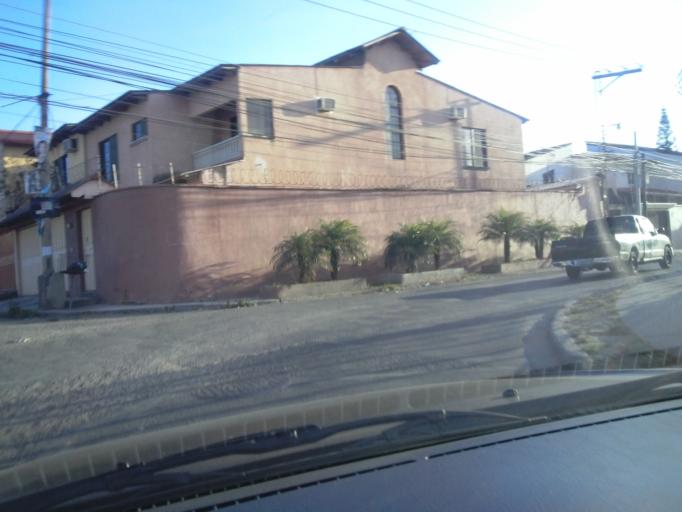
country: HN
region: Francisco Morazan
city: Yaguacire
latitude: 14.0509
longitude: -87.2293
